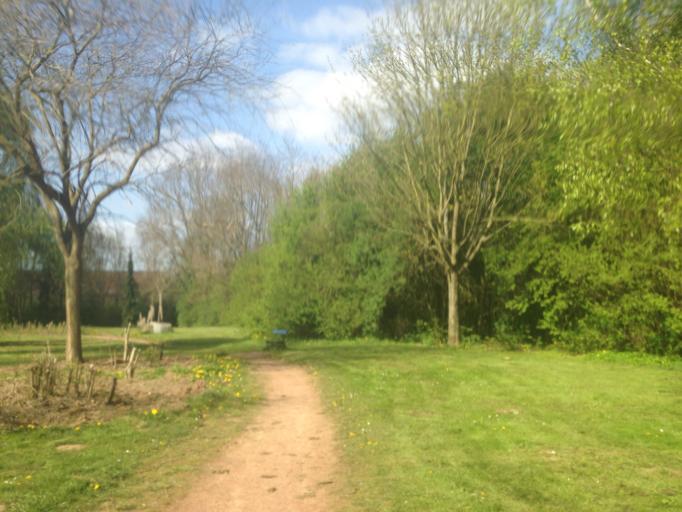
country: FR
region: Nord-Pas-de-Calais
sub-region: Departement du Pas-de-Calais
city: Avion
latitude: 50.4074
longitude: 2.8378
